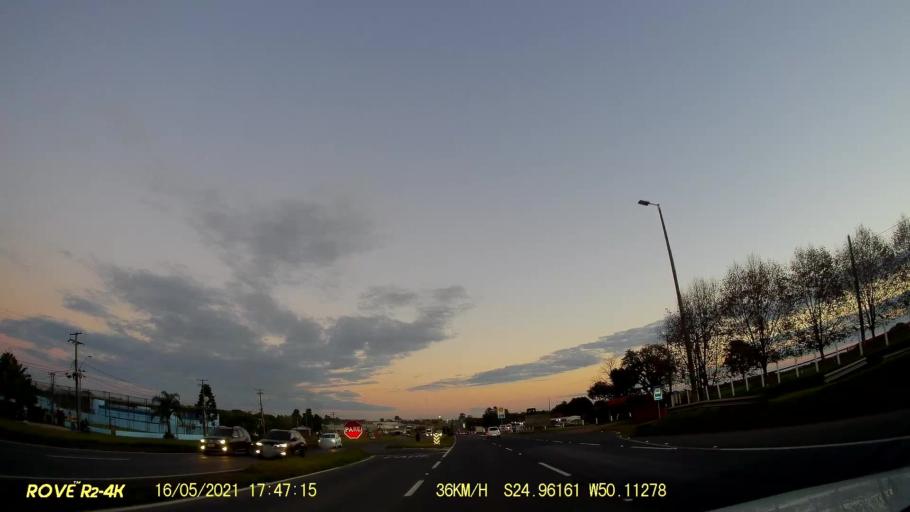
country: BR
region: Parana
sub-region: Carambei
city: Carambei
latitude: -24.9616
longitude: -50.1128
